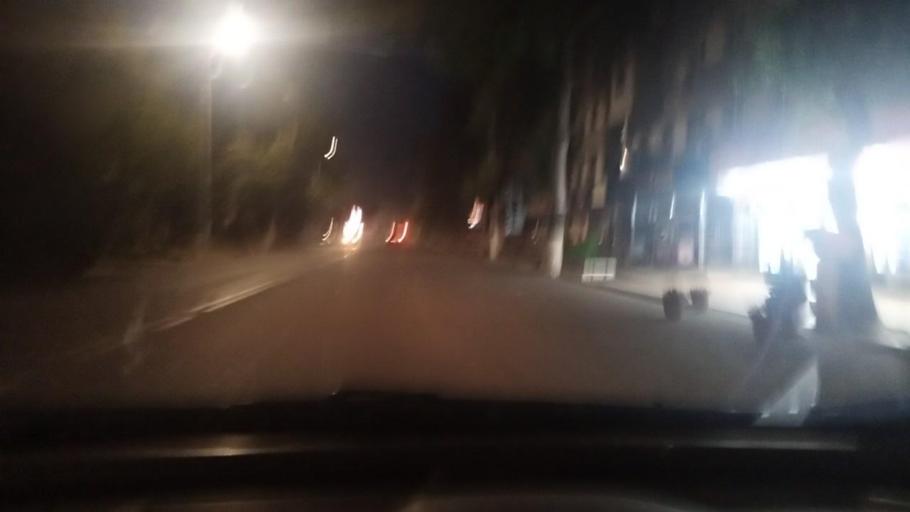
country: UZ
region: Toshkent Shahri
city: Tashkent
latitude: 41.2730
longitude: 69.2783
